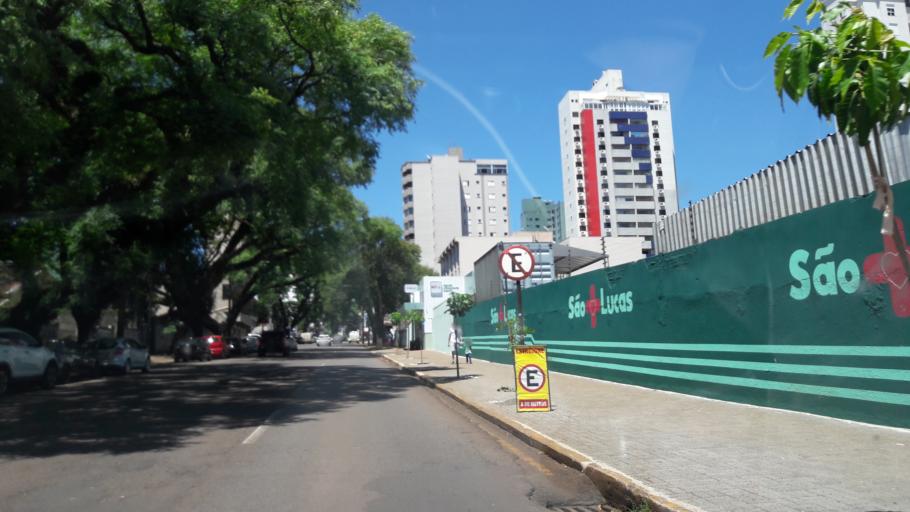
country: BR
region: Parana
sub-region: Cascavel
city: Cascavel
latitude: -24.9507
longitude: -53.4490
